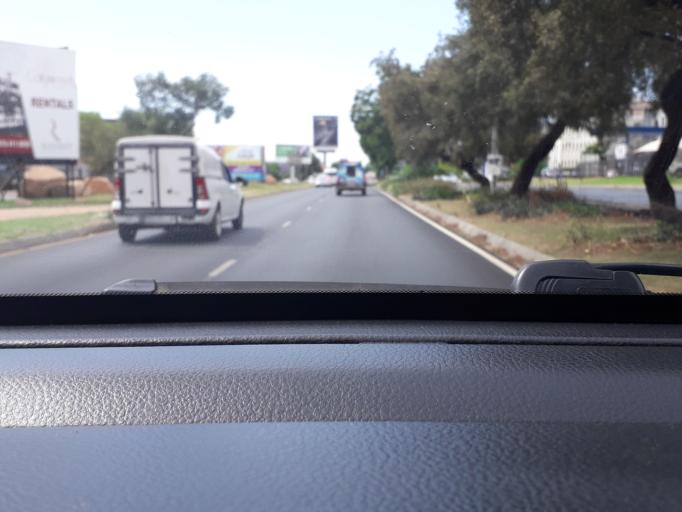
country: ZA
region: Gauteng
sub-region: City of Johannesburg Metropolitan Municipality
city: Midrand
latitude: -26.0505
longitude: 28.0587
